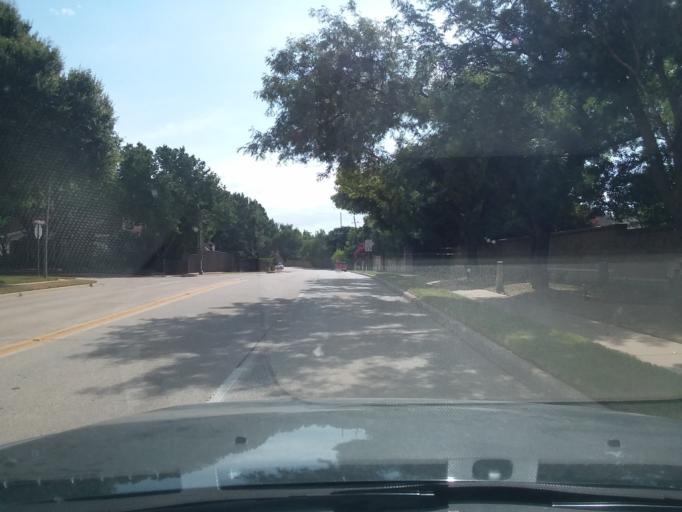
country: US
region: Texas
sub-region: Denton County
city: Flower Mound
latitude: 33.0137
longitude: -97.0792
